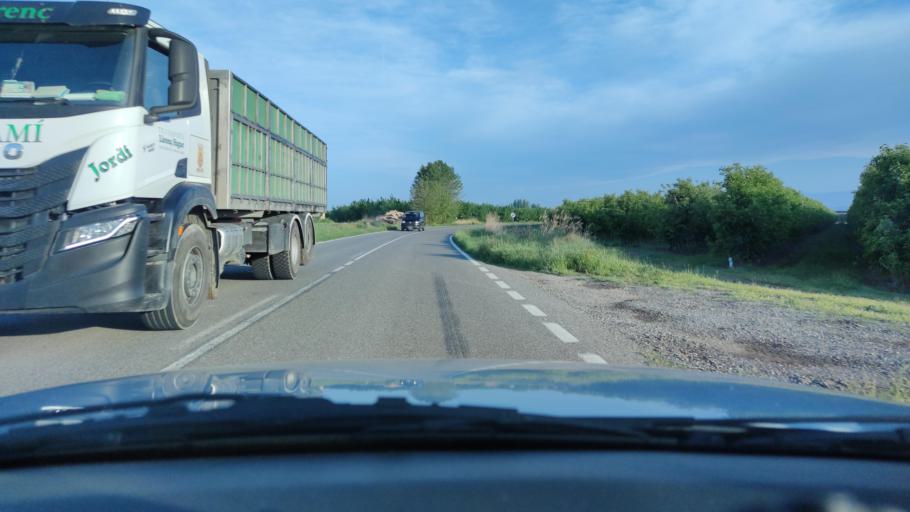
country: ES
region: Catalonia
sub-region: Provincia de Lleida
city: Ivars d'Urgell
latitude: 41.6929
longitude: 0.9874
